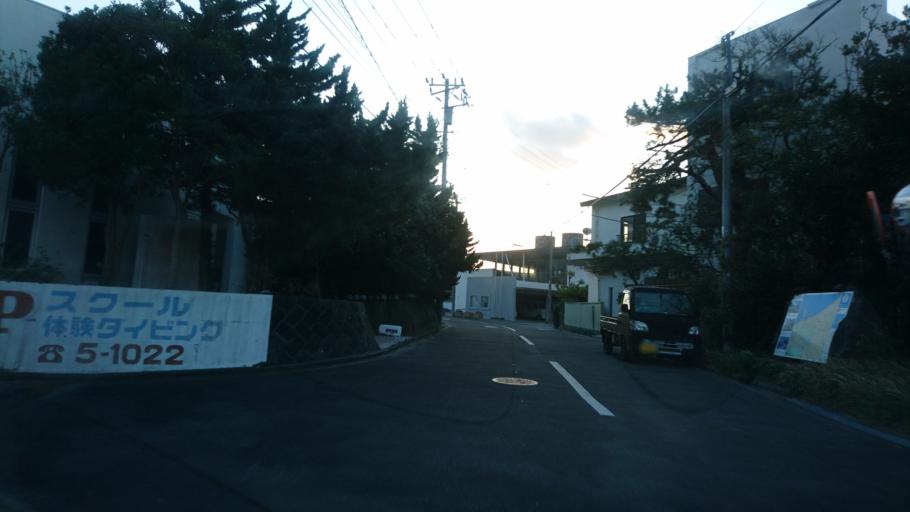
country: JP
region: Shizuoka
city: Shimoda
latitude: 34.3730
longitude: 139.2537
